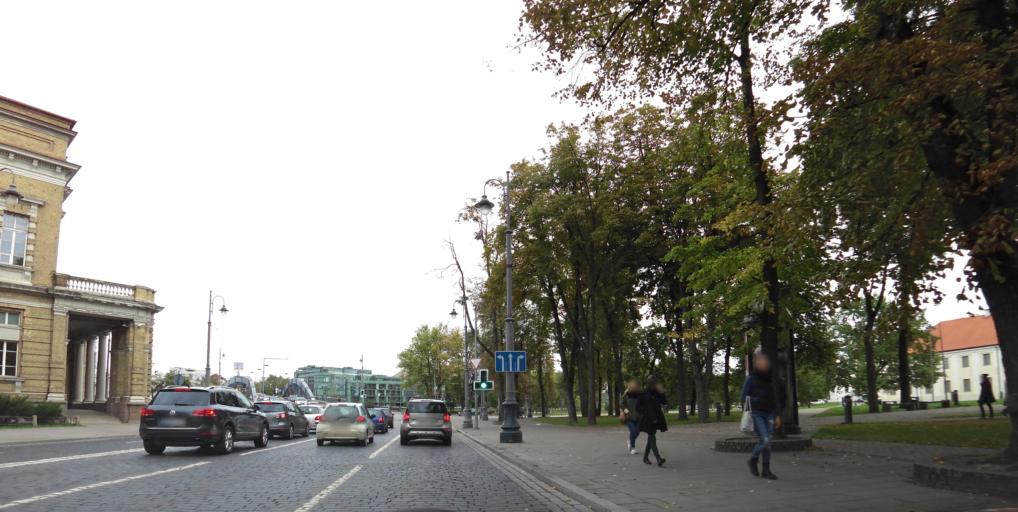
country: LT
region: Vilnius County
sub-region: Vilnius
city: Vilnius
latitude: 54.6876
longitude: 25.2876
